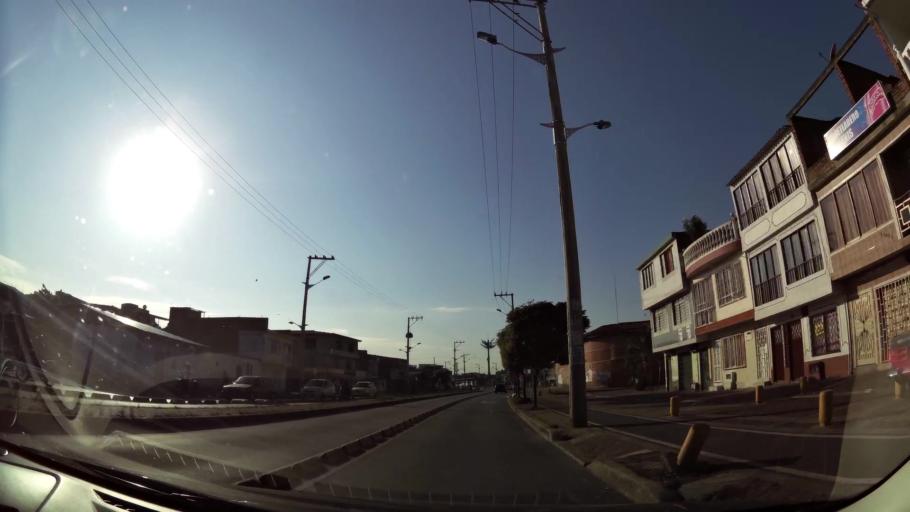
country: CO
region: Valle del Cauca
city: Cali
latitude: 3.4287
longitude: -76.5065
